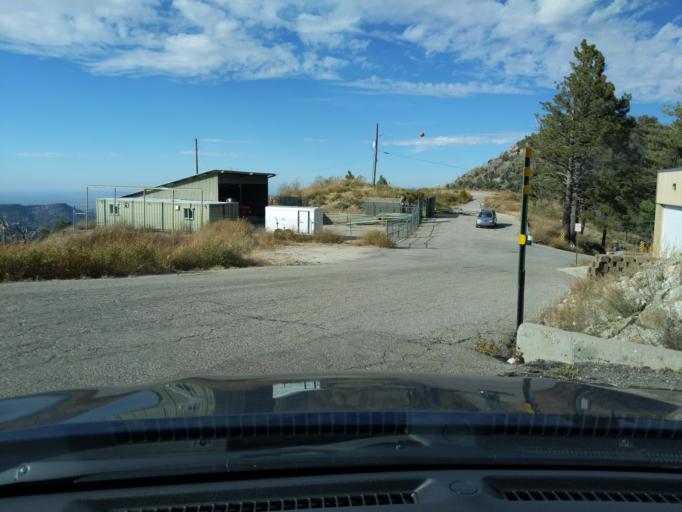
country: US
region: Arizona
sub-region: Pinal County
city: Oracle
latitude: 32.4489
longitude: -110.7547
